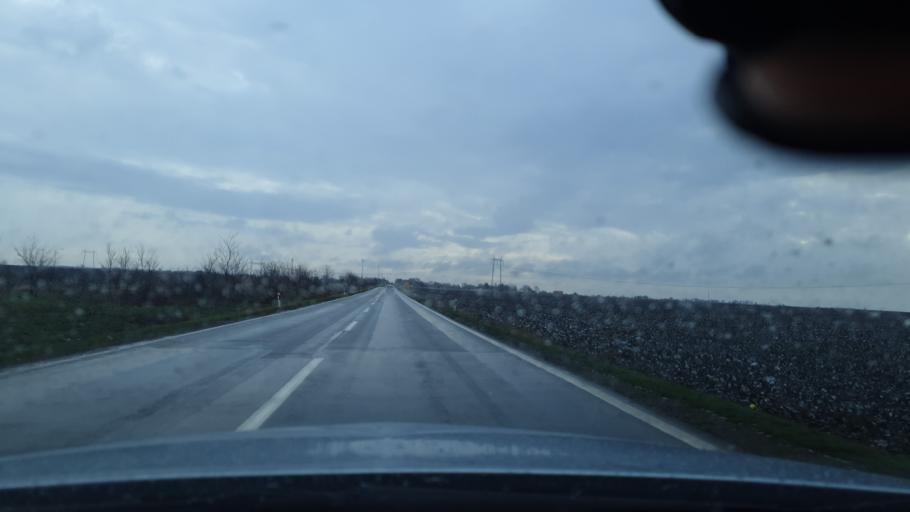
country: RS
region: Autonomna Pokrajina Vojvodina
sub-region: Juznobanatski Okrug
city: Kovin
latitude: 44.8275
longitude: 20.8431
